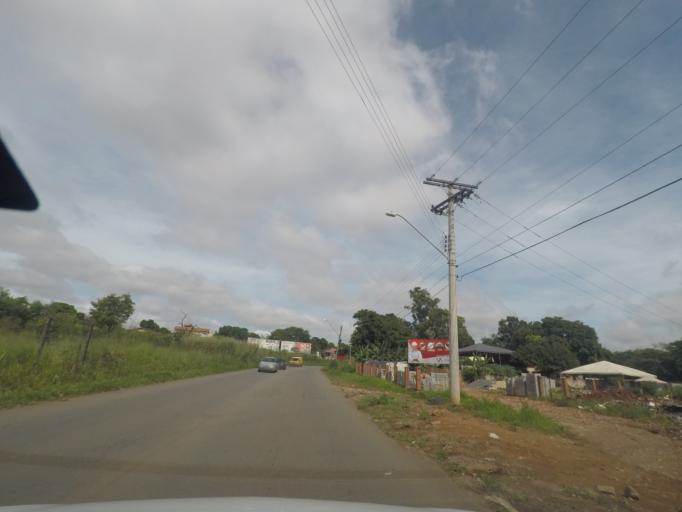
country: BR
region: Goias
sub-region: Goiania
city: Goiania
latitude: -16.6725
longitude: -49.2049
